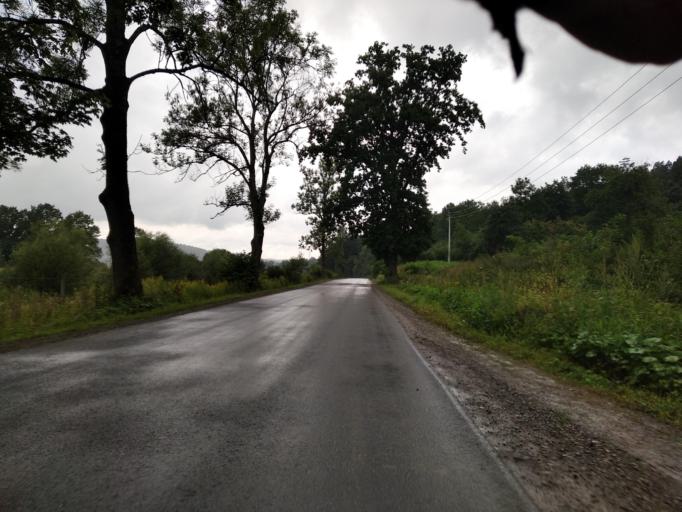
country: PL
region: Subcarpathian Voivodeship
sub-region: Powiat brzozowski
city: Dydnia
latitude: 49.6793
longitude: 22.2676
